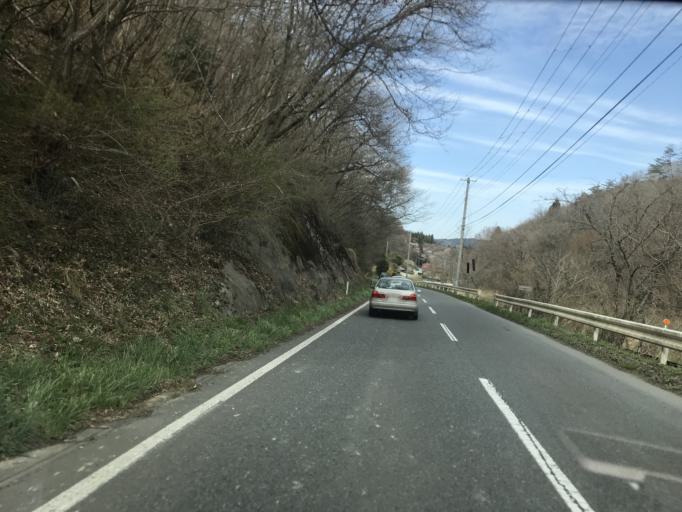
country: JP
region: Iwate
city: Ichinoseki
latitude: 38.8250
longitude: 141.3296
